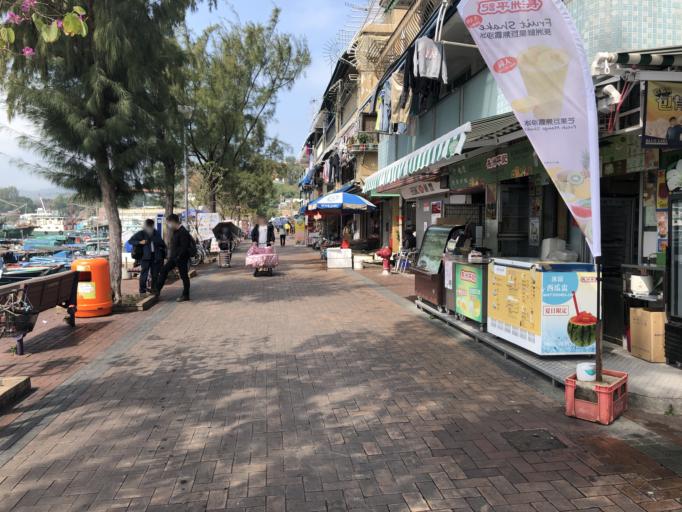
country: HK
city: Yung Shue Wan
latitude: 22.2106
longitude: 114.0281
